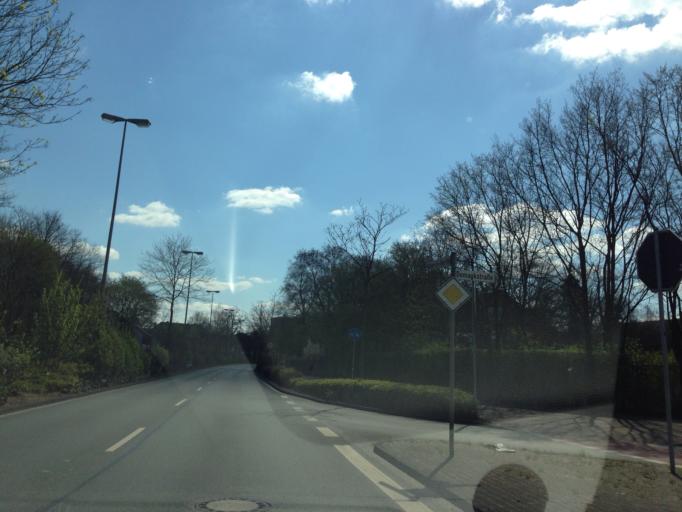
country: DE
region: North Rhine-Westphalia
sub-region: Regierungsbezirk Munster
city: Muenster
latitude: 51.9637
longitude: 7.6017
